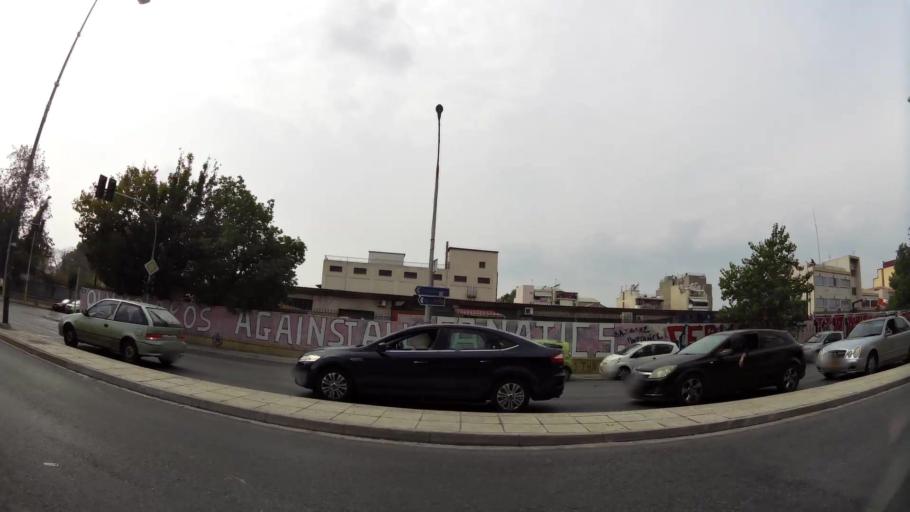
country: GR
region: Attica
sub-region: Nomos Piraios
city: Agios Ioannis Rentis
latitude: 37.9503
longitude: 23.6636
